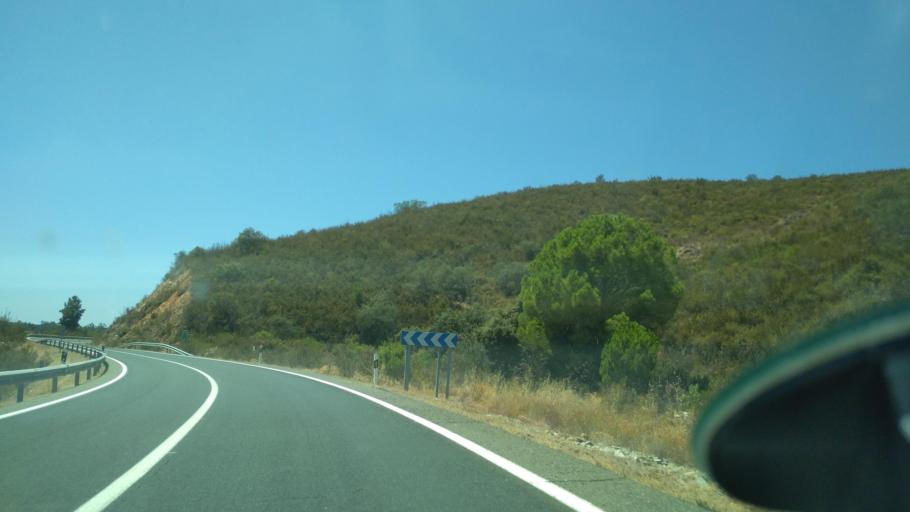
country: ES
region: Andalusia
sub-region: Provincia de Huelva
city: Aracena
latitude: 37.8565
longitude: -6.5631
